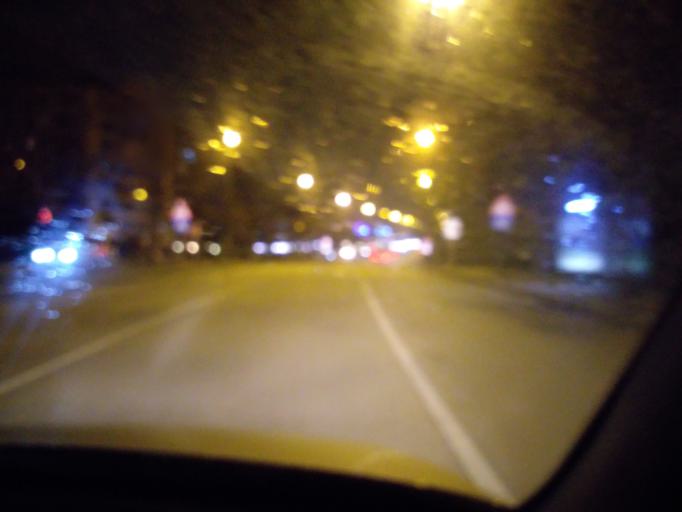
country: TR
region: Ankara
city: Batikent
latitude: 39.8816
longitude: 32.7118
